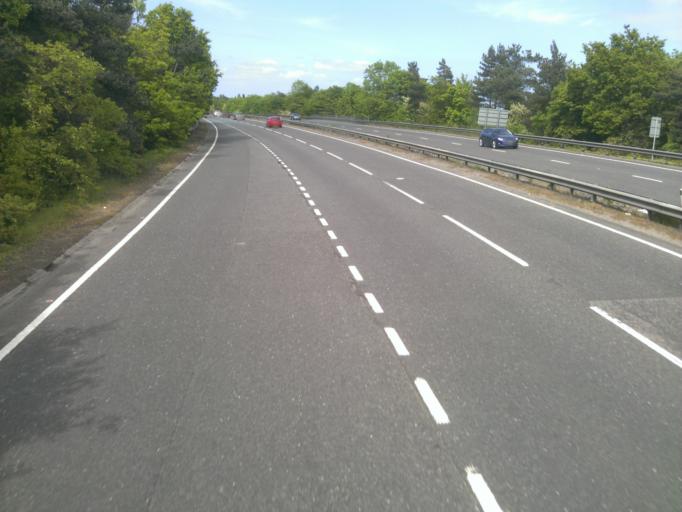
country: GB
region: England
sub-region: Essex
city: Colchester
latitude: 51.9279
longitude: 0.9420
